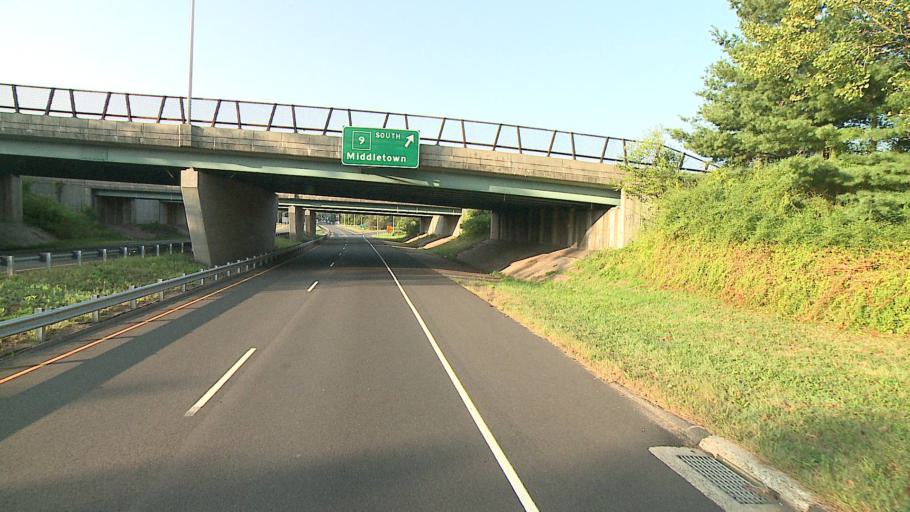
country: US
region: Connecticut
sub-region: Hartford County
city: Kensington
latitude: 41.6257
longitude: -72.7409
